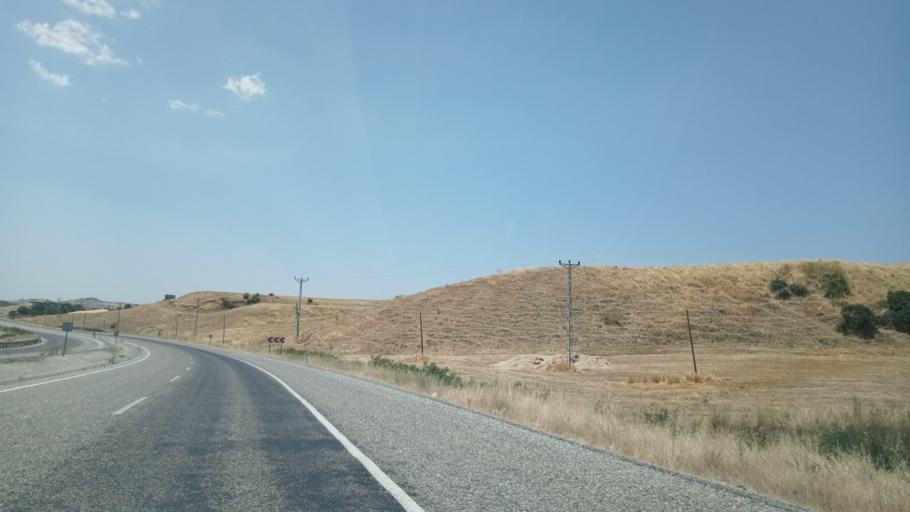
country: TR
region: Batman
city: Bekirhan
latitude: 38.1553
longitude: 41.3227
